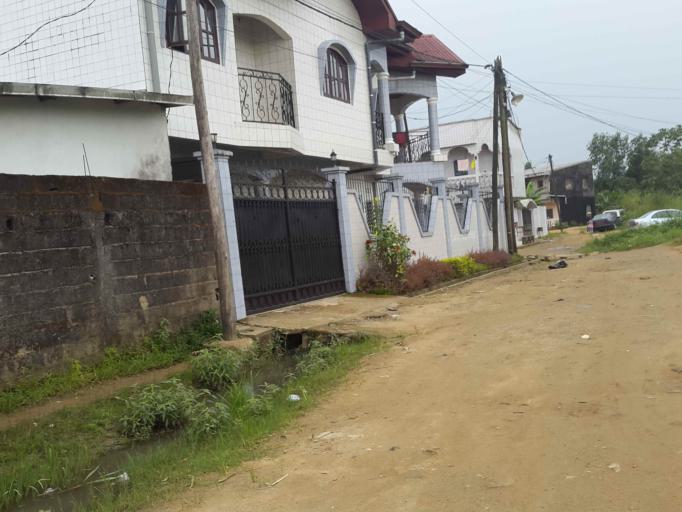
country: CM
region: Littoral
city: Douala
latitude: 4.0939
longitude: 9.7278
